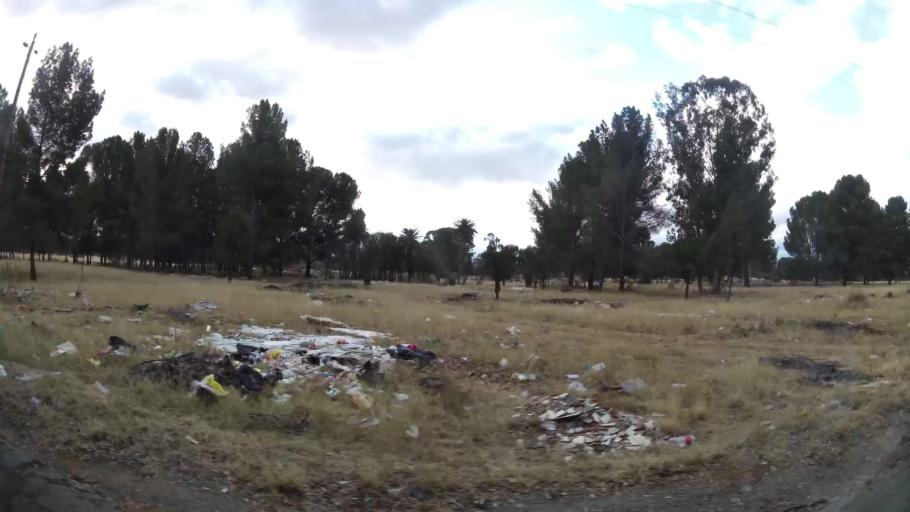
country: ZA
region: Orange Free State
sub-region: Lejweleputswa District Municipality
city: Welkom
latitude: -27.9999
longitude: 26.7182
